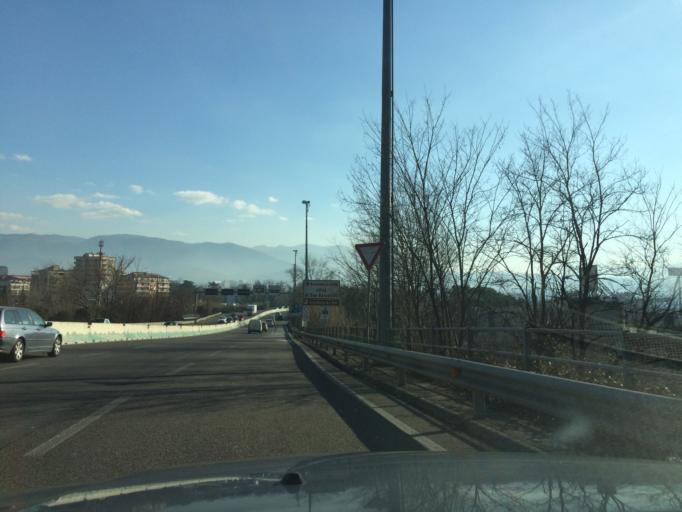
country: IT
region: Umbria
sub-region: Provincia di Terni
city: Terni
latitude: 42.5726
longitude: 12.6289
